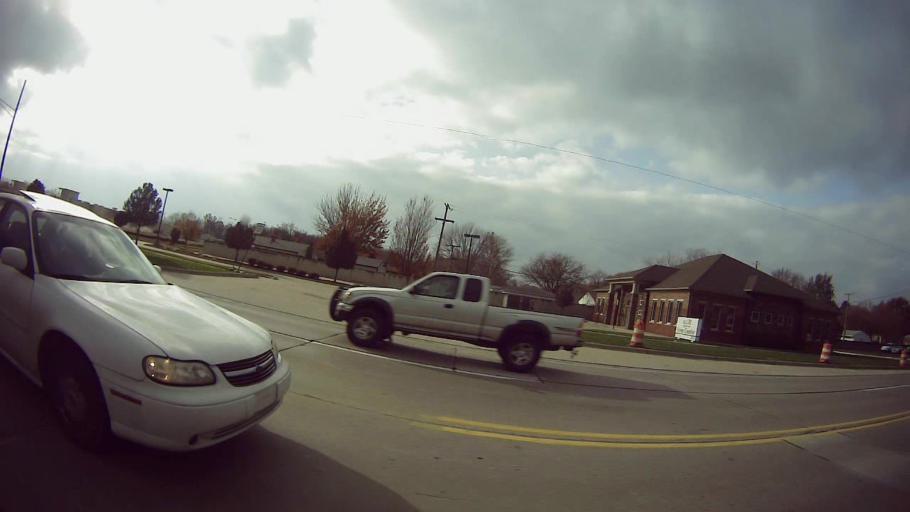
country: US
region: Michigan
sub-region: Macomb County
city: Eastpointe
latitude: 42.4824
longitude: -82.9868
